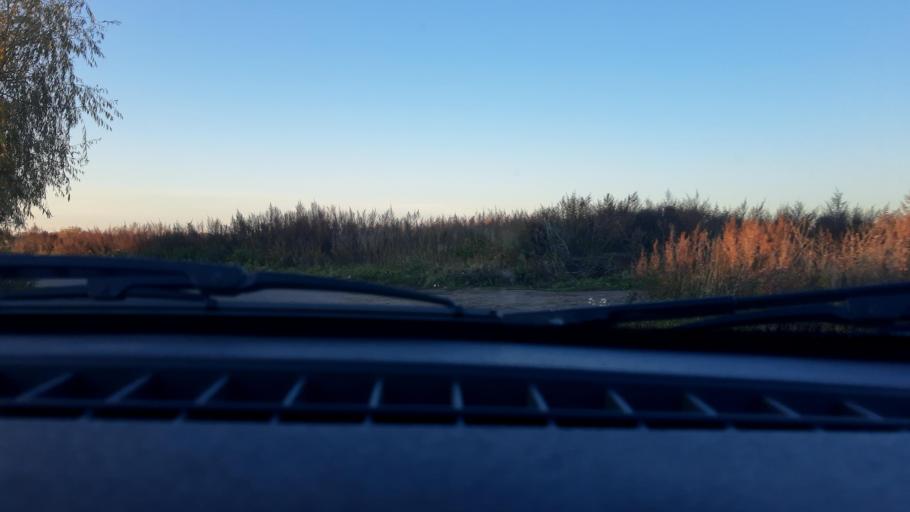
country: RU
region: Bashkortostan
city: Ufa
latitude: 54.8584
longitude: 56.0228
